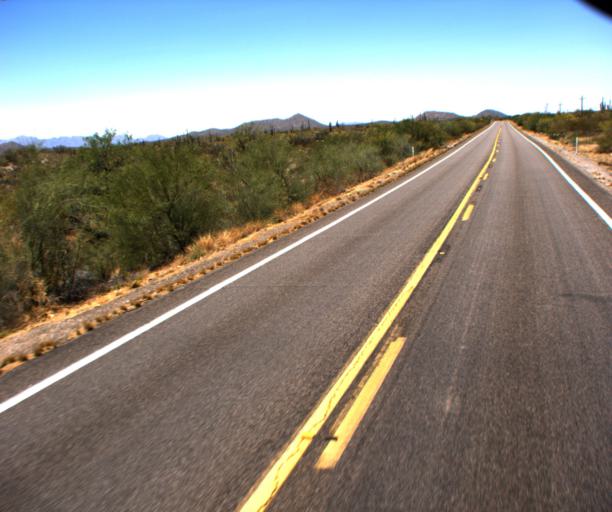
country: US
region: Arizona
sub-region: Pima County
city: Catalina
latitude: 32.7013
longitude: -111.0919
